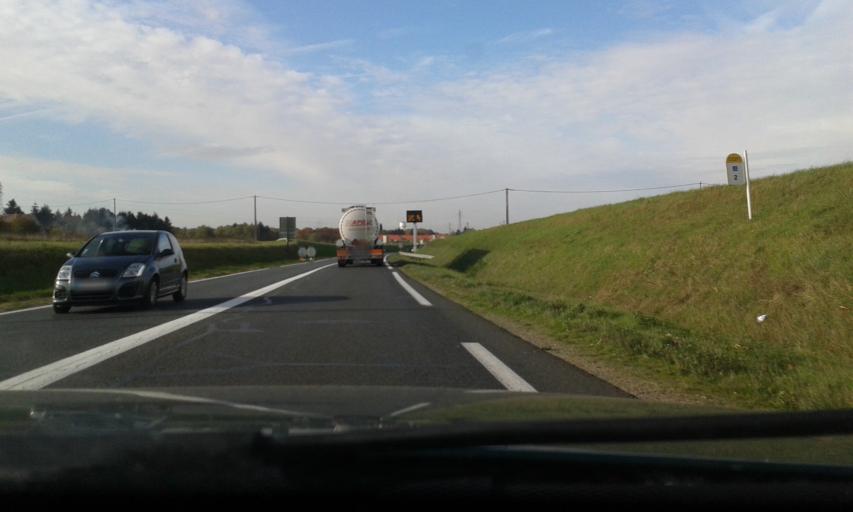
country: FR
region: Centre
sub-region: Departement du Loiret
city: Olivet
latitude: 47.8430
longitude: 1.8991
